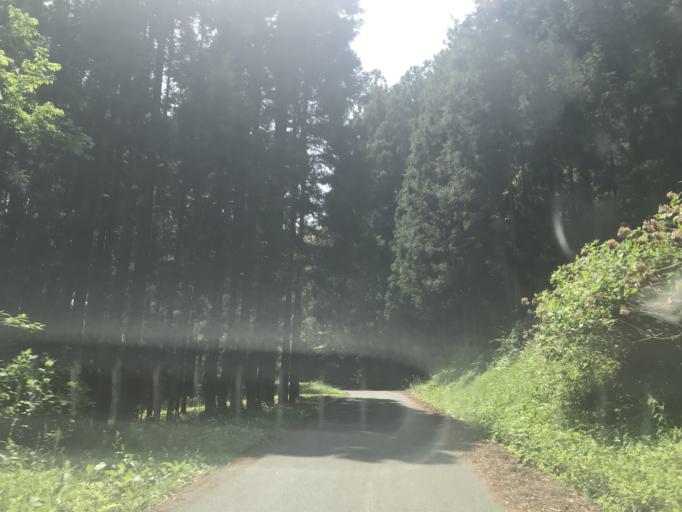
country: JP
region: Iwate
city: Ichinoseki
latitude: 38.9627
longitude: 141.2389
